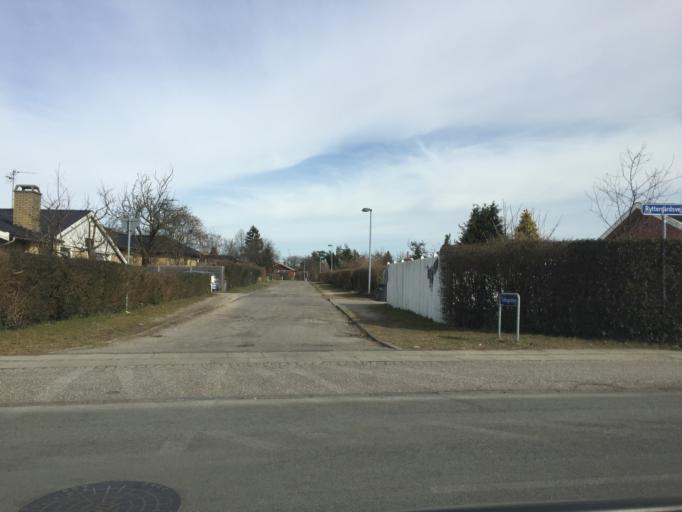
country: DK
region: Capital Region
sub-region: Fureso Kommune
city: Farum
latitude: 55.8156
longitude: 12.3650
